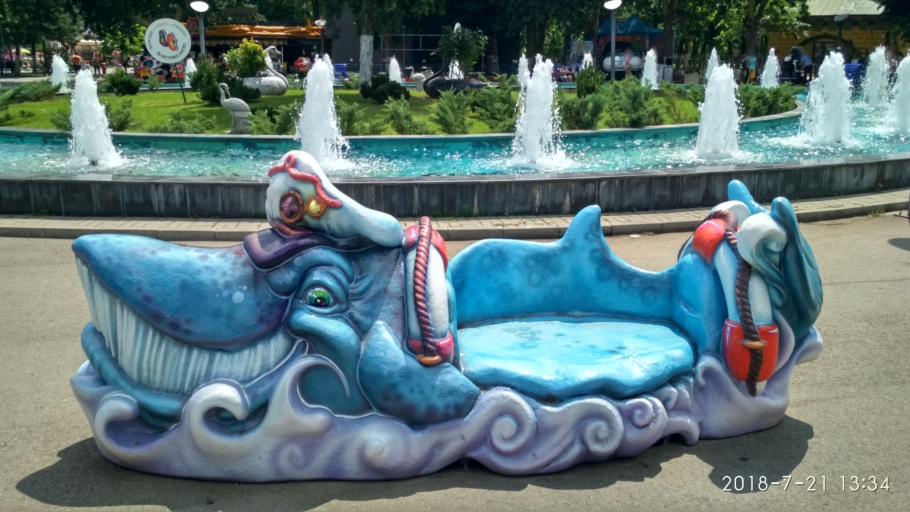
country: RO
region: Bucuresti
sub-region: Municipiul Bucuresti
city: Bucuresti
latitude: 44.4008
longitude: 26.1082
